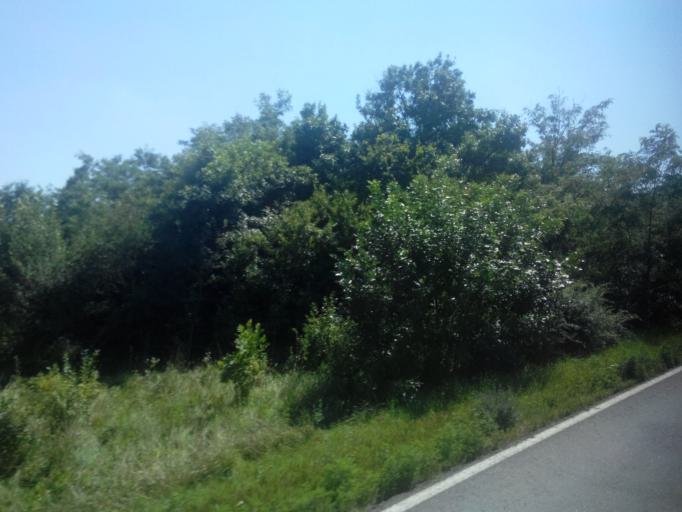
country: RO
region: Timis
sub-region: Comuna Barna
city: Barna
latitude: 45.7635
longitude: 22.0235
